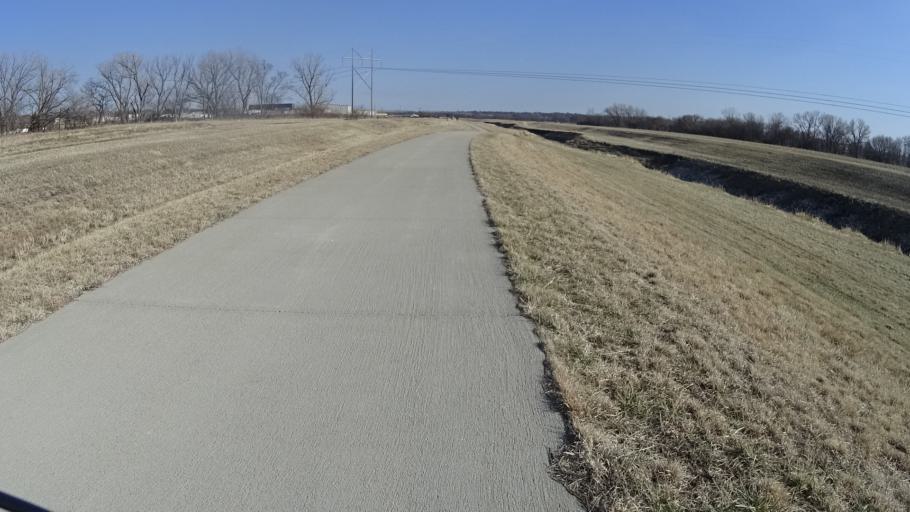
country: US
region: Nebraska
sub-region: Sarpy County
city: Papillion
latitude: 41.1703
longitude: -96.0756
